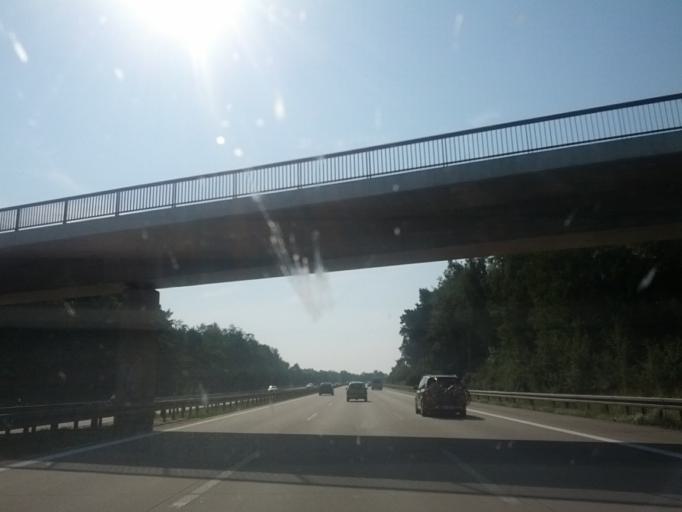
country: DE
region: Brandenburg
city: Ahrensfelde
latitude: 52.5826
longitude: 13.6332
